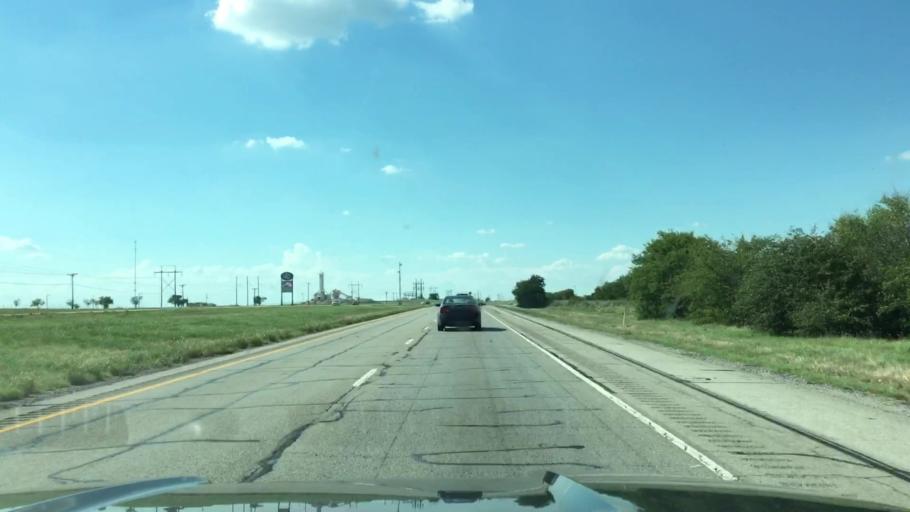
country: US
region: Texas
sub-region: Wise County
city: Decatur
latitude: 33.1734
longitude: -97.5404
